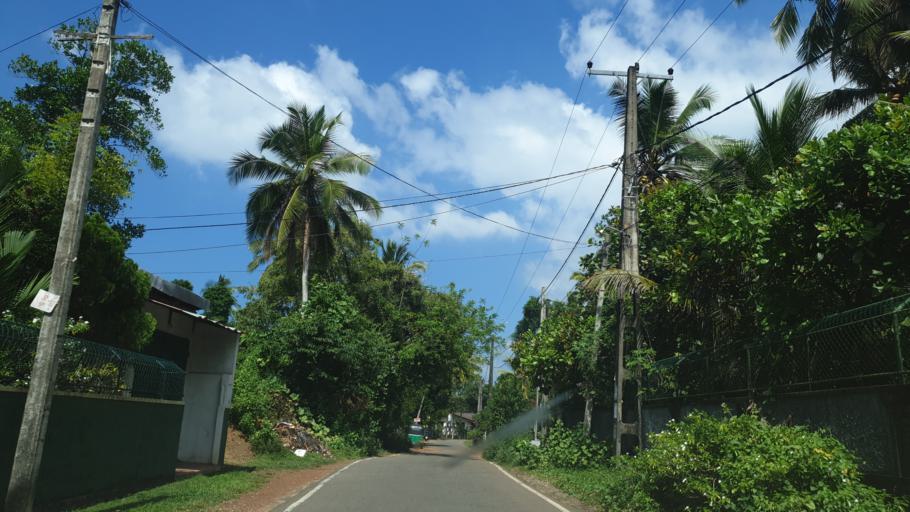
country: LK
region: Western
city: Panadura
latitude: 6.6754
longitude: 79.9394
